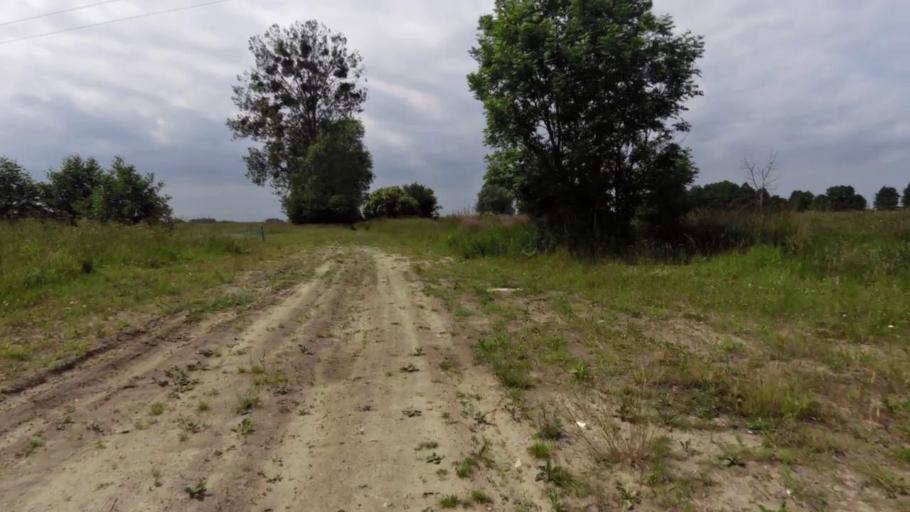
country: PL
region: West Pomeranian Voivodeship
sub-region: Powiat goleniowski
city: Stepnica
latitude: 53.7280
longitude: 14.6434
